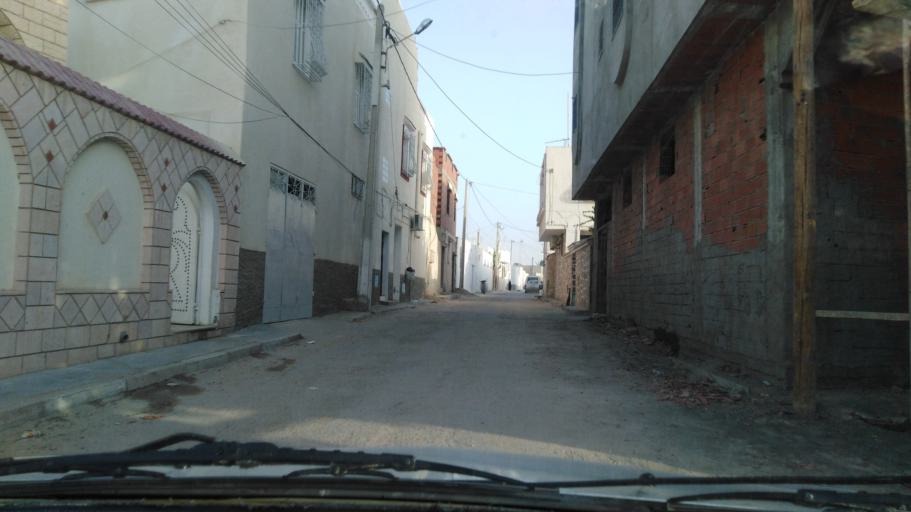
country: TN
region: Qabis
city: Gabes
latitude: 33.9594
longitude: 9.9968
